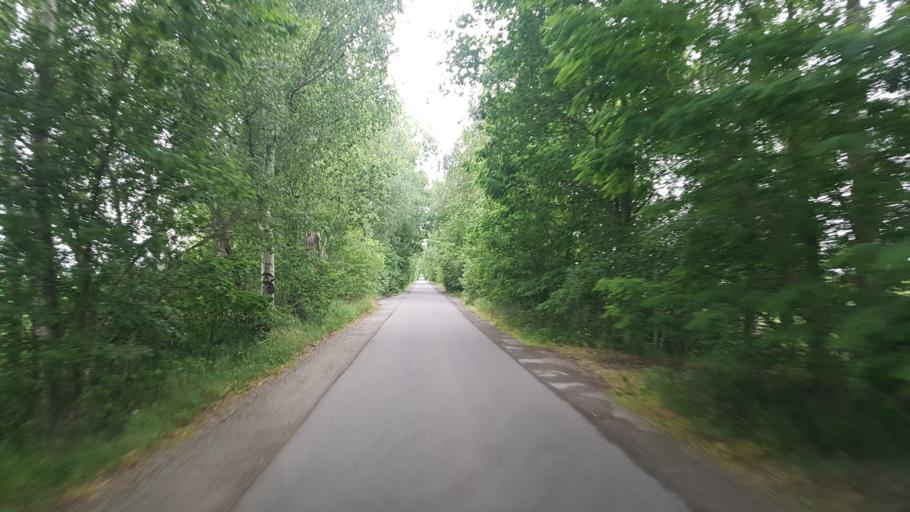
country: DE
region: Brandenburg
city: Schraden
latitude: 51.4327
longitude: 13.6938
